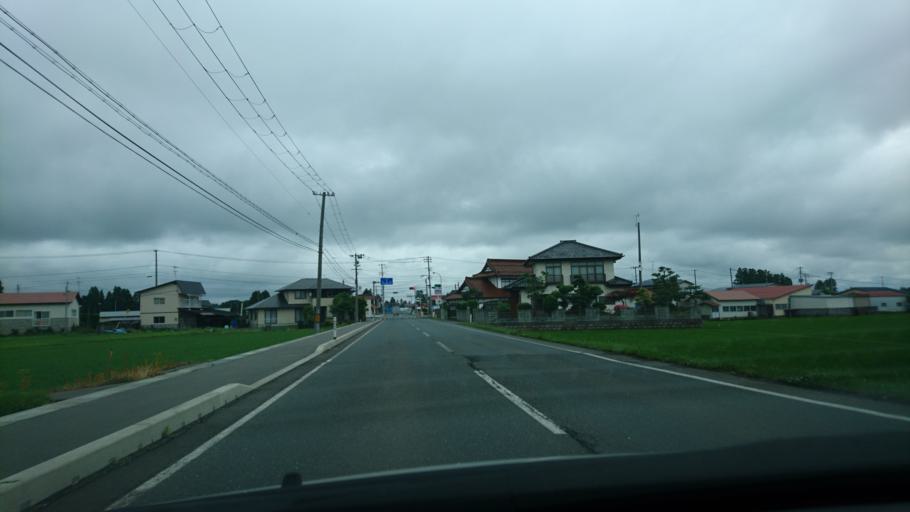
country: JP
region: Iwate
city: Mizusawa
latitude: 39.1284
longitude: 141.0531
